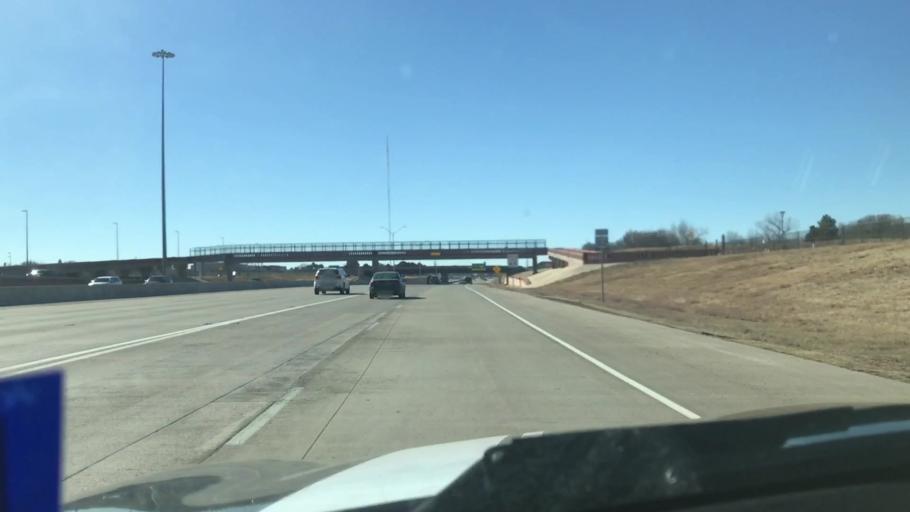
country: US
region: Texas
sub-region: Lubbock County
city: Lubbock
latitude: 33.5901
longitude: -101.8806
